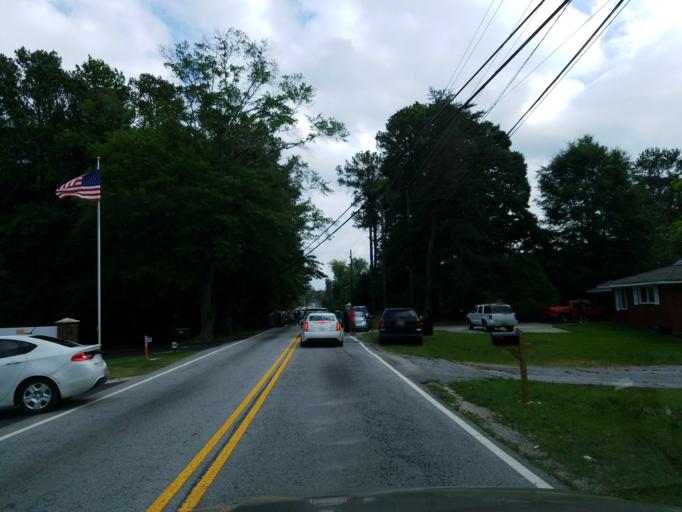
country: US
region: Georgia
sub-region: Douglas County
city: Lithia Springs
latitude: 33.7841
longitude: -84.6559
